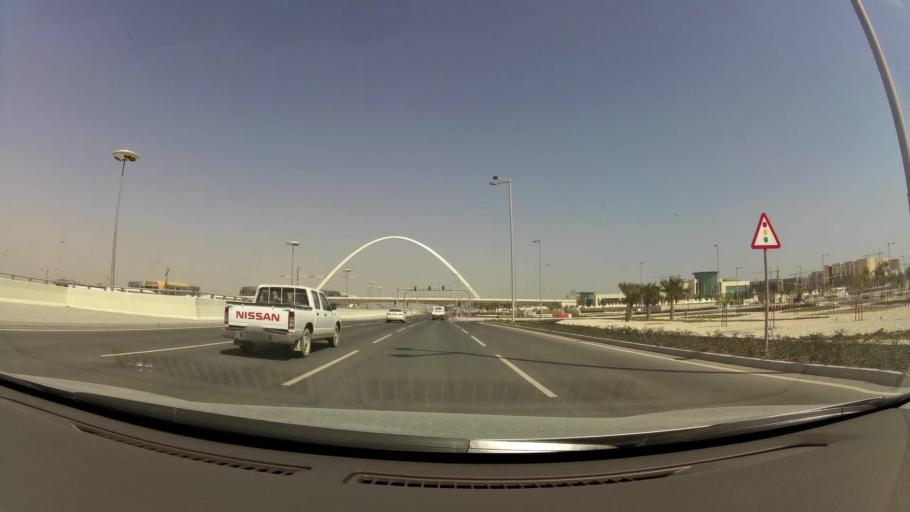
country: QA
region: Baladiyat Umm Salal
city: Umm Salal Muhammad
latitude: 25.3971
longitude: 51.5163
